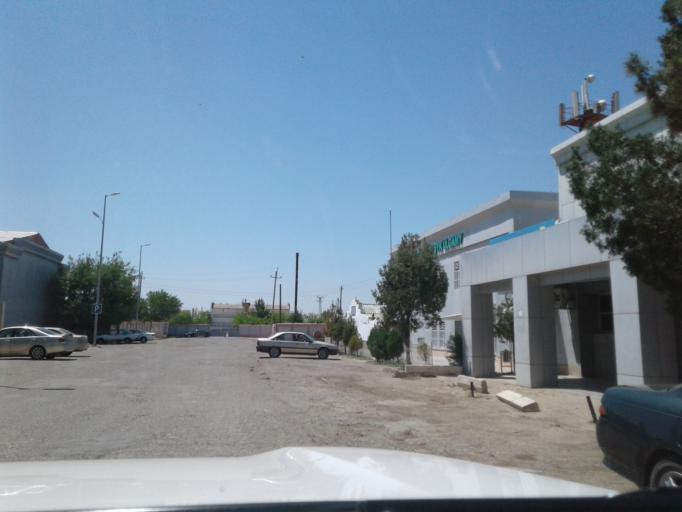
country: TM
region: Mary
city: Mary
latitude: 37.6049
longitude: 61.9239
